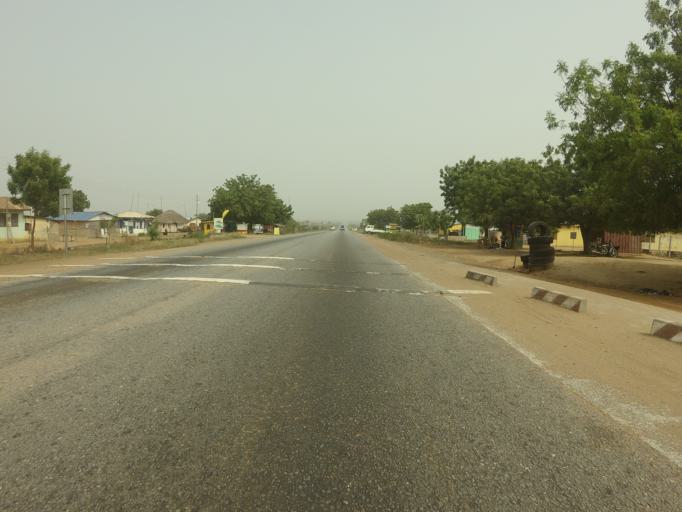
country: GH
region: Greater Accra
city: Tema
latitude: 5.8662
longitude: 0.2917
